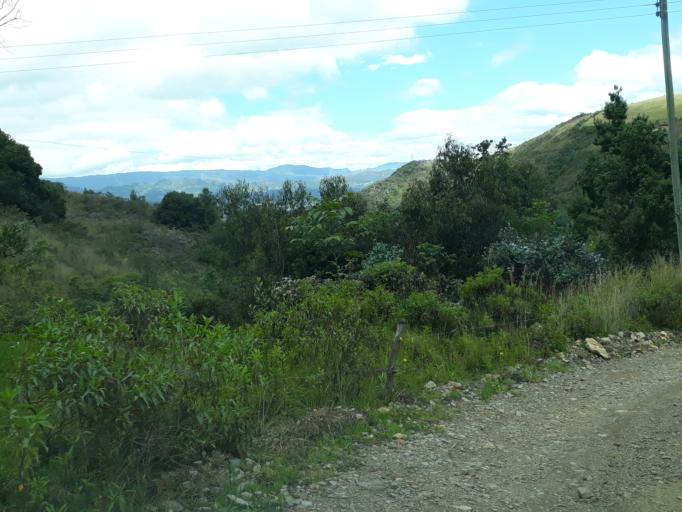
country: CO
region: Cundinamarca
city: Guacheta
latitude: 5.4377
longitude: -73.7037
